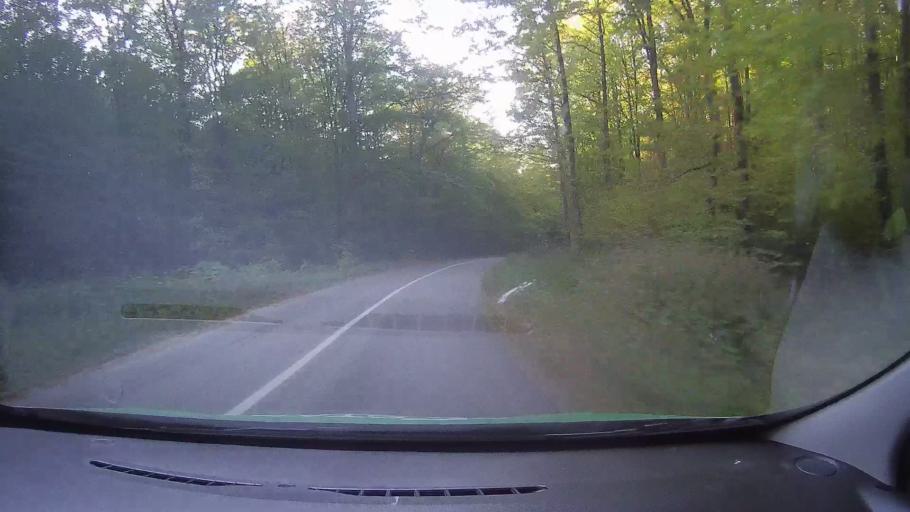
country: RO
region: Timis
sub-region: Comuna Nadrag
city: Nadrag
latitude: 45.6774
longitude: 22.1604
